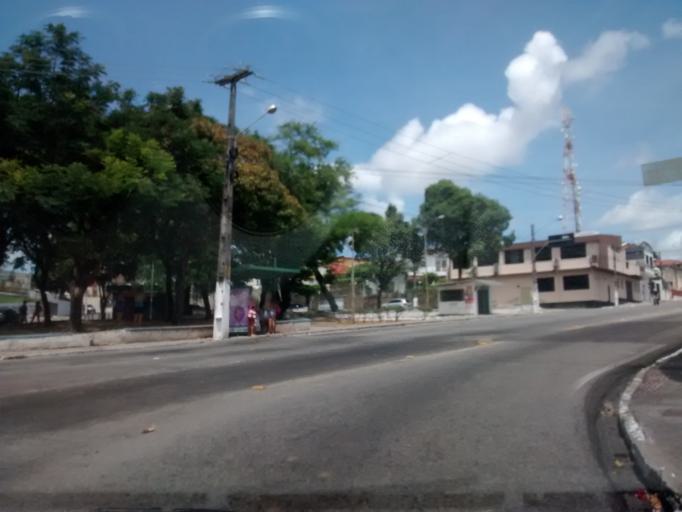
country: BR
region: Rio Grande do Norte
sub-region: Natal
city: Natal
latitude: -5.7913
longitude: -35.2095
